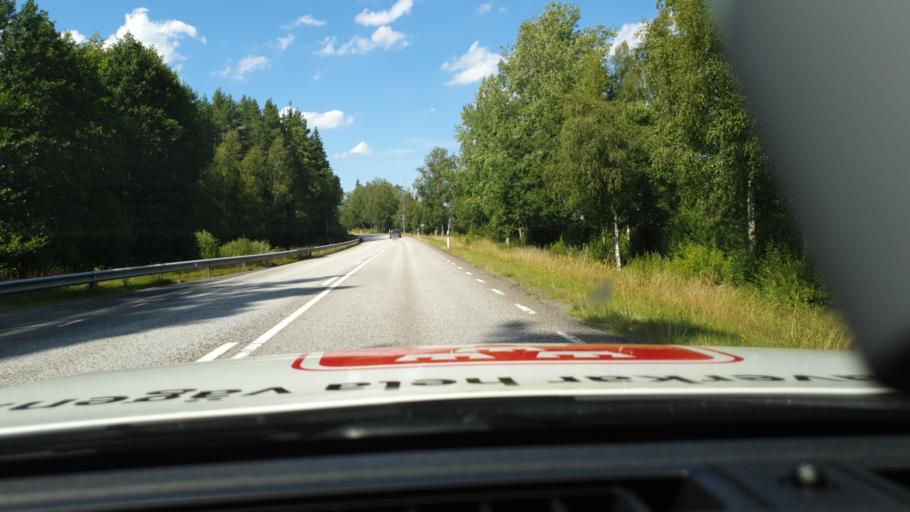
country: SE
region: Joenkoeping
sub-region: Vaggeryds Kommun
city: Vaggeryd
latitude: 57.5394
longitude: 14.2675
